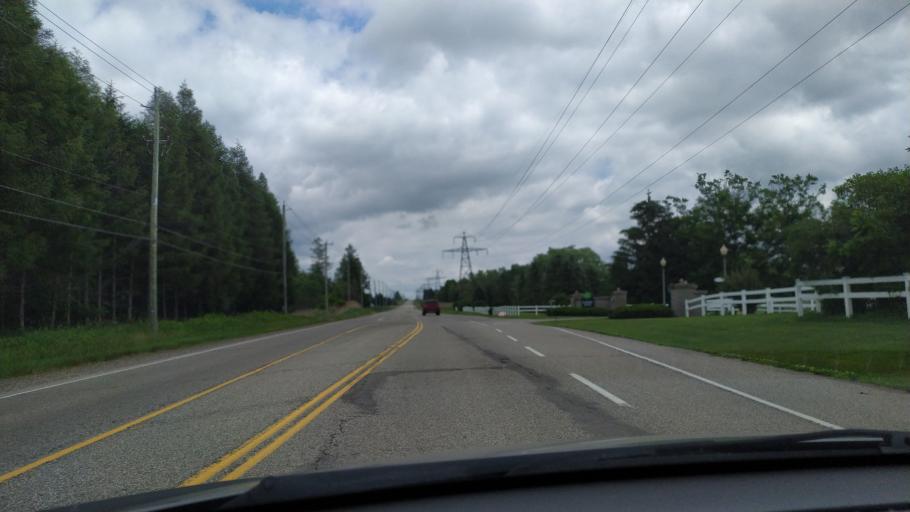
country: CA
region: Ontario
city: Waterloo
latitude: 43.4232
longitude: -80.7046
